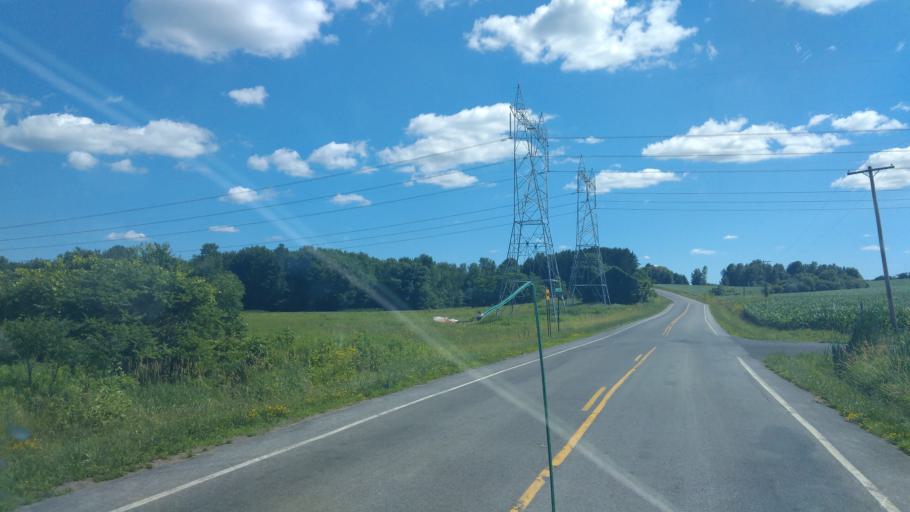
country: US
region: New York
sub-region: Wayne County
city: Lyons
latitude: 43.1329
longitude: -77.0147
